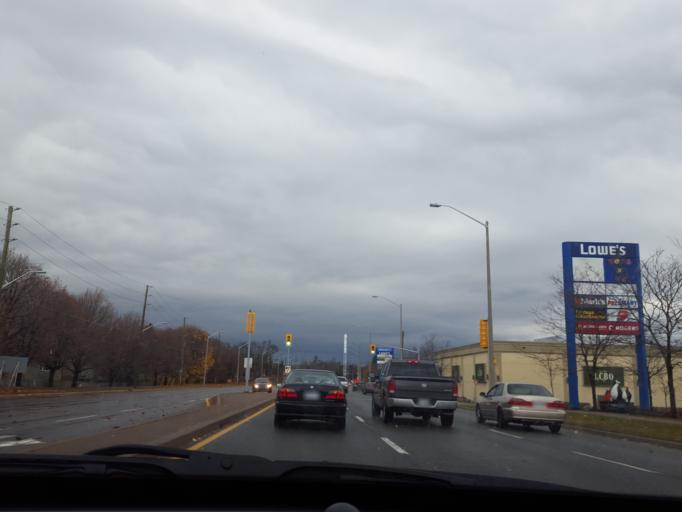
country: CA
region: Ontario
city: Ajax
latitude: 43.8445
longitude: -79.0726
